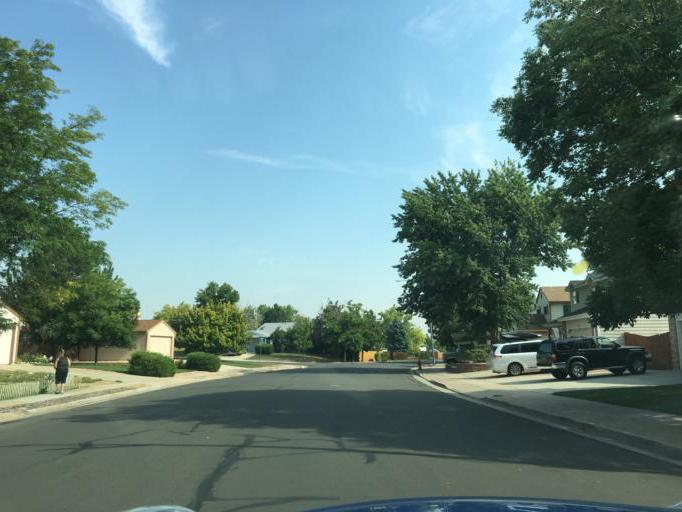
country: US
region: Colorado
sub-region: Adams County
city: Westminster
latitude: 39.8316
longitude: -105.0589
